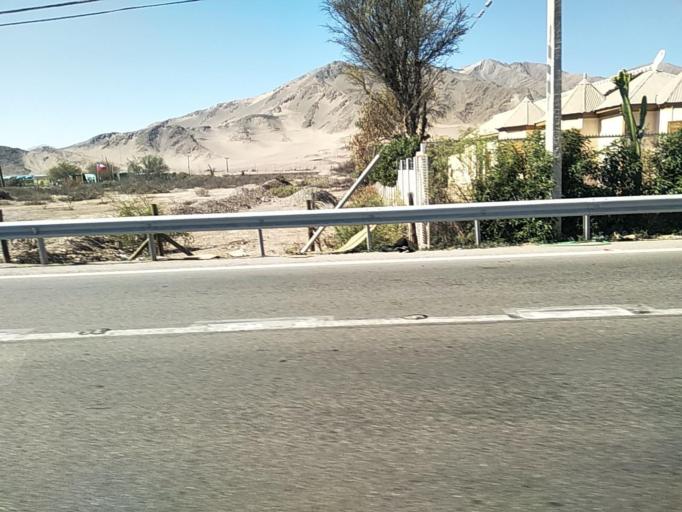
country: CL
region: Atacama
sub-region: Provincia de Copiapo
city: Copiapo
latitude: -27.3420
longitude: -70.3652
